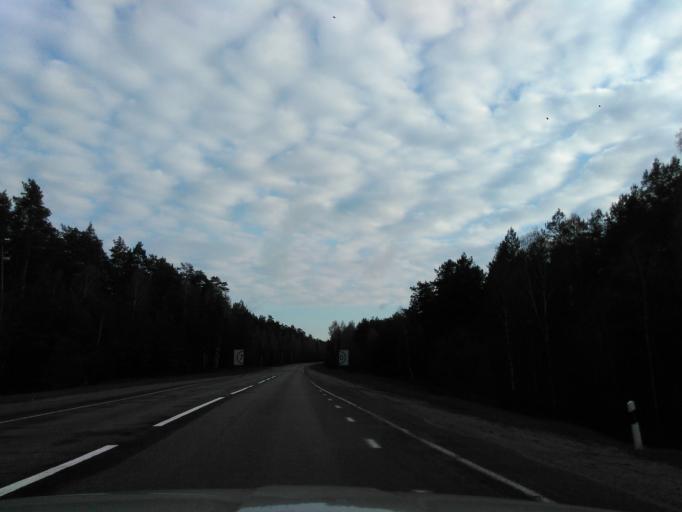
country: BY
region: Minsk
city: Plyeshchanitsy
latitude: 54.3473
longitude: 27.8794
